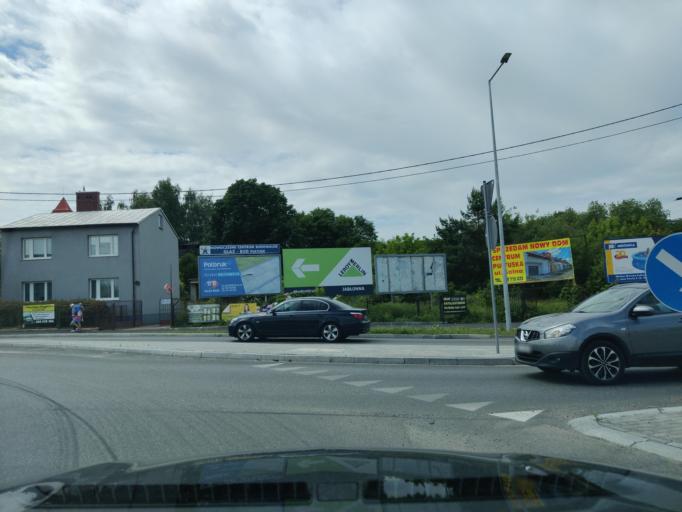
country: PL
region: Masovian Voivodeship
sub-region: Powiat pultuski
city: Pultusk
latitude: 52.6977
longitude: 21.0854
